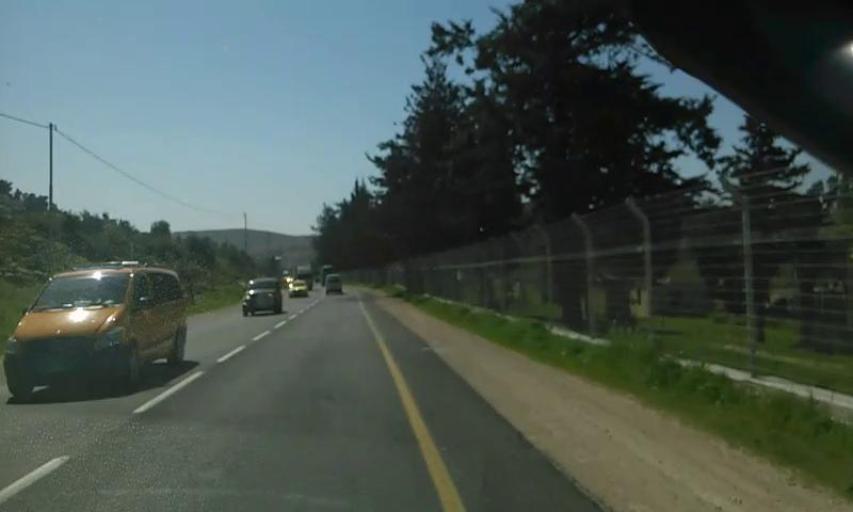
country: PS
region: West Bank
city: Shuyukh al `Arrub
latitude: 31.6313
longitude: 35.1321
